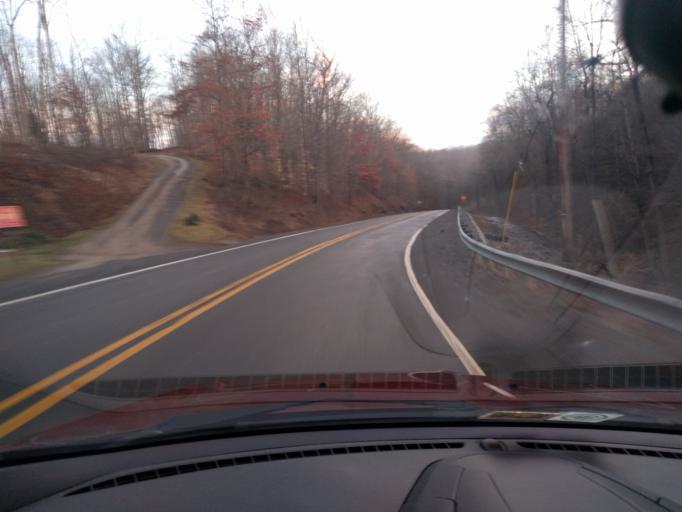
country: US
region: West Virginia
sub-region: Greenbrier County
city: Rainelle
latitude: 38.0238
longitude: -80.9165
